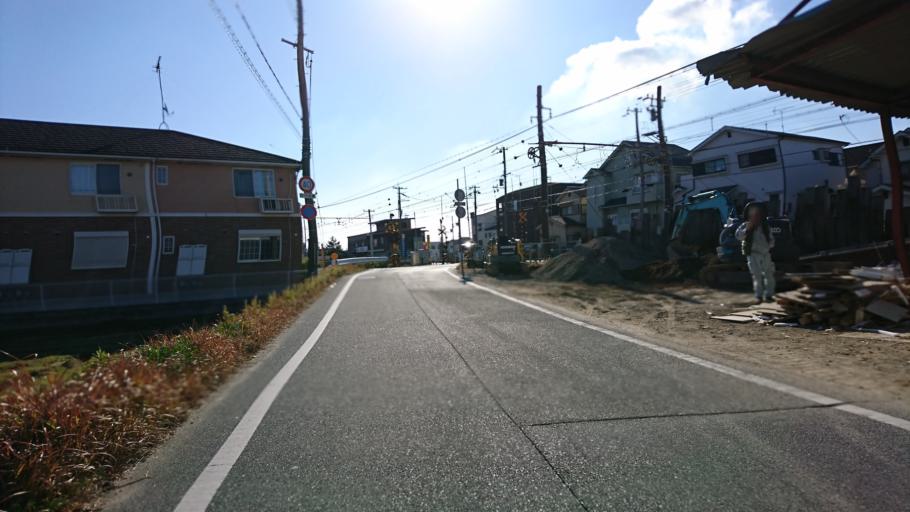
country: JP
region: Hyogo
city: Kakogawacho-honmachi
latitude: 34.7340
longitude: 134.8448
